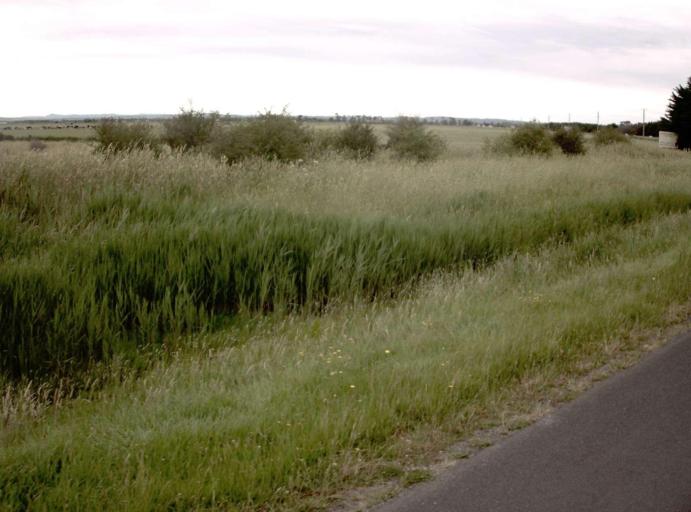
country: AU
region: Victoria
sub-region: Cardinia
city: Koo-Wee-Rup
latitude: -38.2324
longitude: 145.5108
